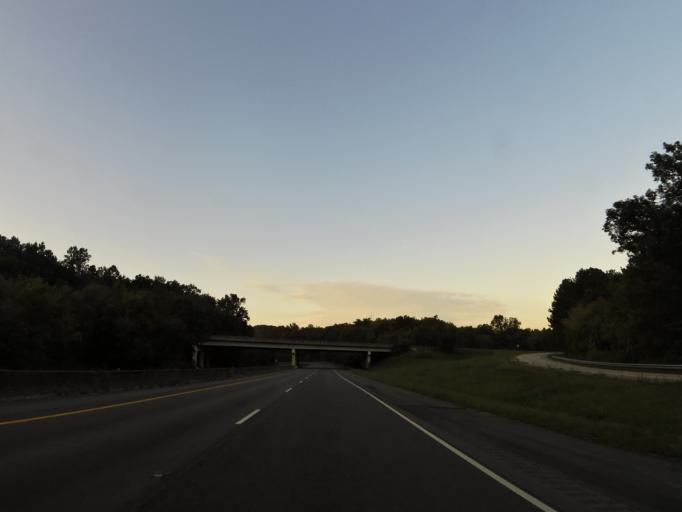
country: US
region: Tennessee
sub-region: Morgan County
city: Coalfield
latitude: 35.9425
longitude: -84.3651
